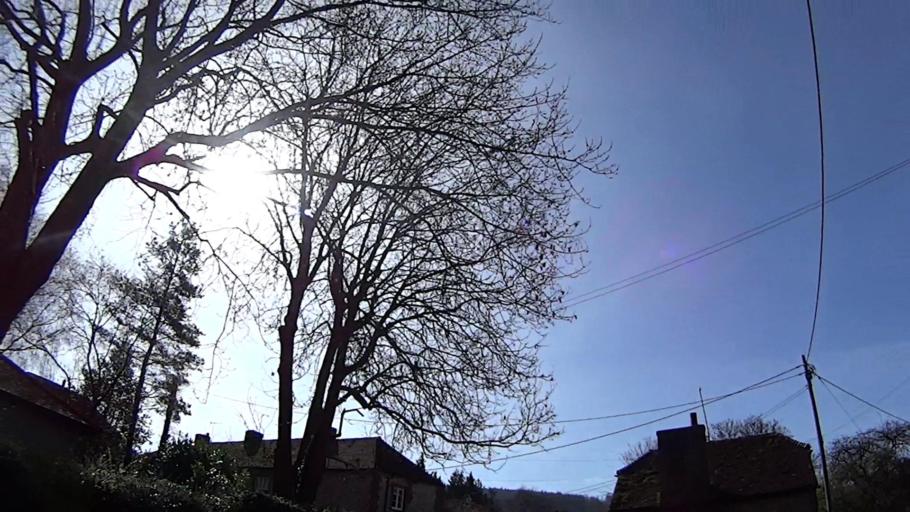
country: GB
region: England
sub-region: West Sussex
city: Boxgrove
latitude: 50.9103
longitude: -0.7388
